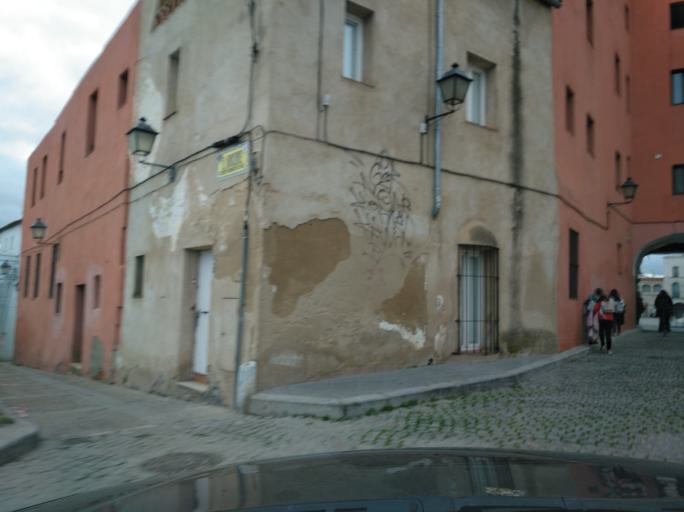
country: ES
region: Extremadura
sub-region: Provincia de Badajoz
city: Badajoz
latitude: 38.8810
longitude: -6.9675
